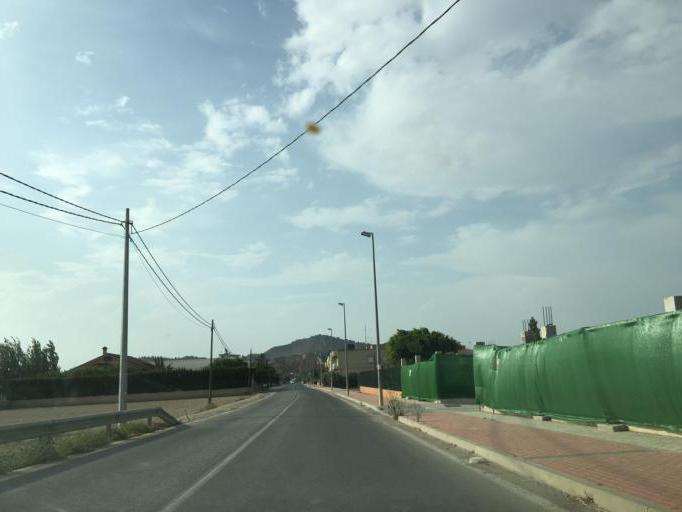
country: ES
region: Murcia
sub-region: Murcia
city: Murcia
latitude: 38.0153
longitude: -1.0829
